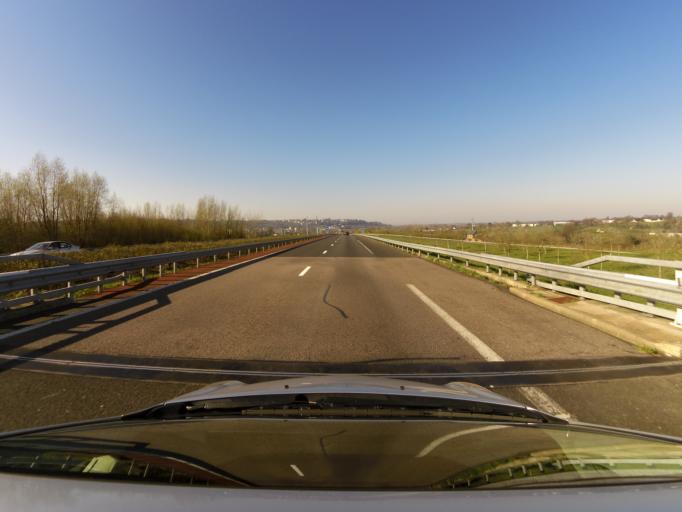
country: FR
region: Lower Normandy
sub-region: Departement de la Manche
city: Saint-Senier-sous-Avranches
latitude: 48.7103
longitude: -1.3297
